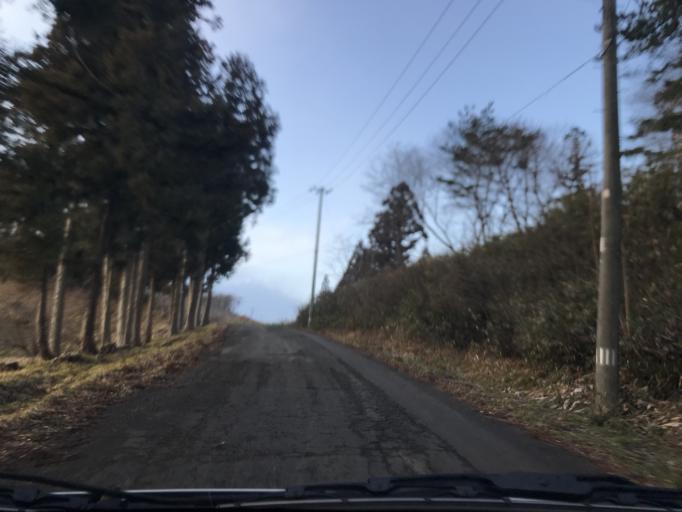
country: JP
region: Iwate
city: Mizusawa
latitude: 39.0365
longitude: 141.1003
